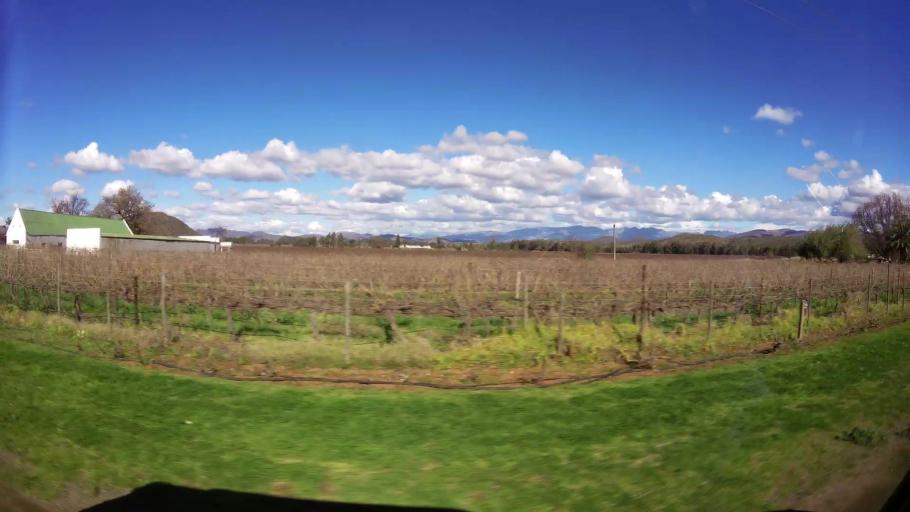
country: ZA
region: Western Cape
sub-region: Cape Winelands District Municipality
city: Ashton
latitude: -33.8067
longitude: 19.8625
